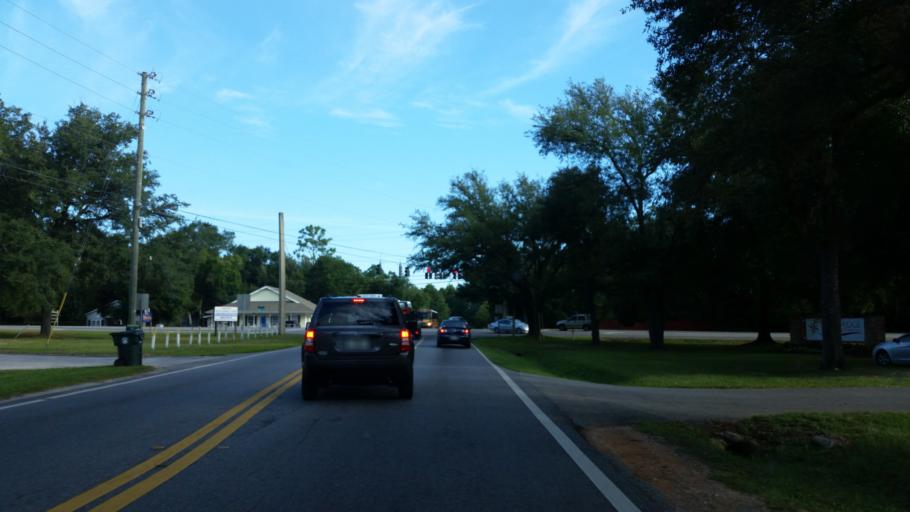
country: US
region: Florida
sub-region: Santa Rosa County
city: Milton
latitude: 30.6303
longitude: -87.0642
